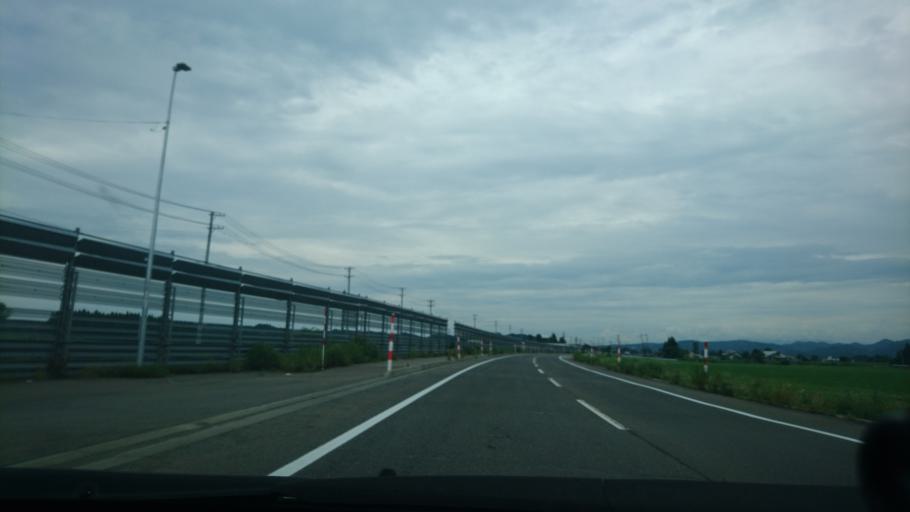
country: JP
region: Akita
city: Omagari
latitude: 39.5120
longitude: 140.3805
